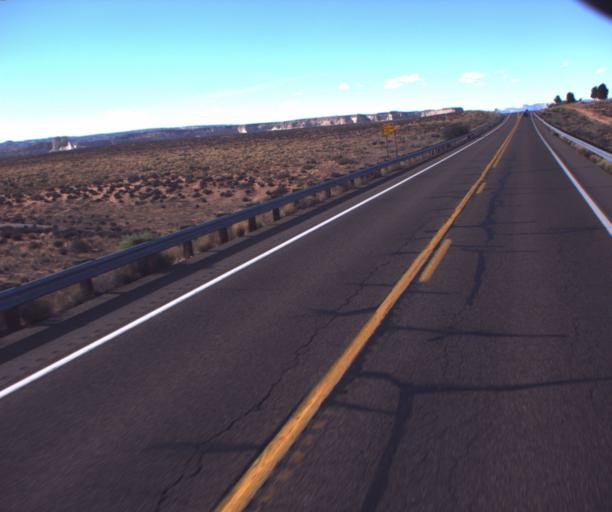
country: US
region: Arizona
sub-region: Coconino County
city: Page
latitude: 36.9875
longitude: -111.5573
